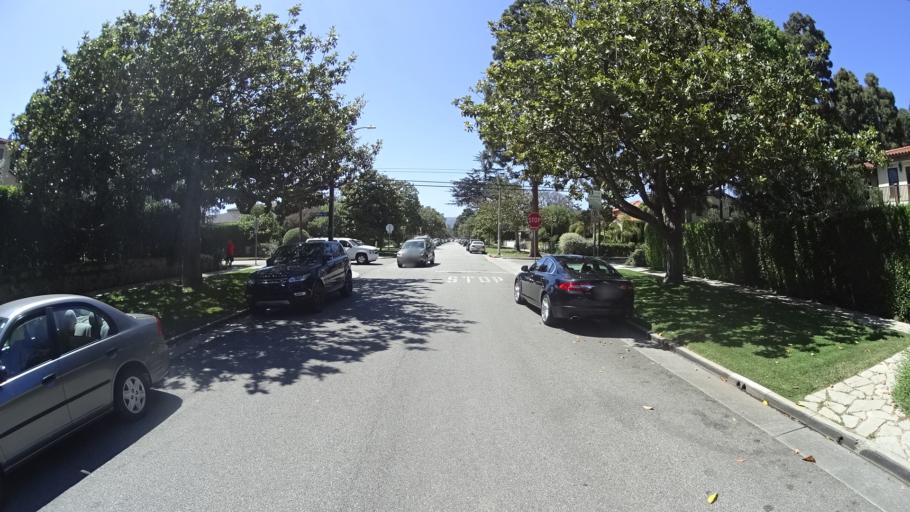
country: US
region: California
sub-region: Los Angeles County
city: Santa Monica
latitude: 34.0355
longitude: -118.4935
